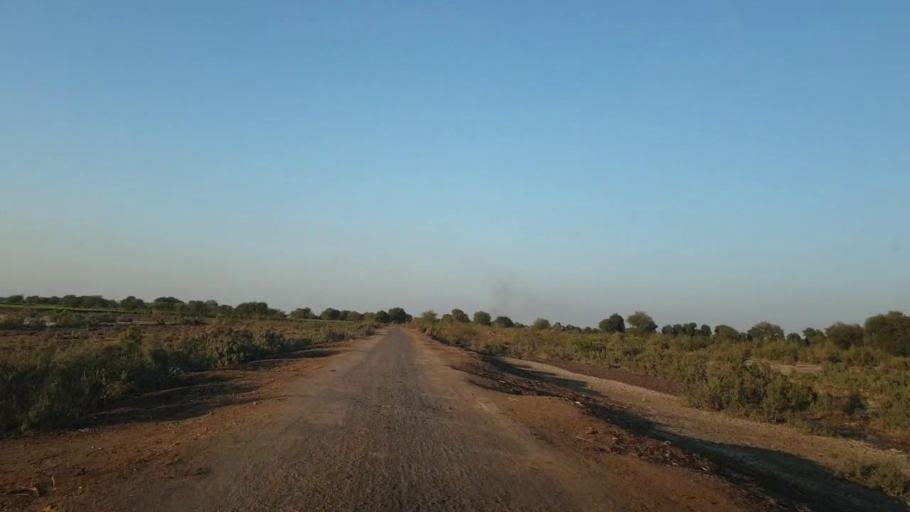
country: PK
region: Sindh
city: Mirpur Khas
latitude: 25.6880
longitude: 69.0504
